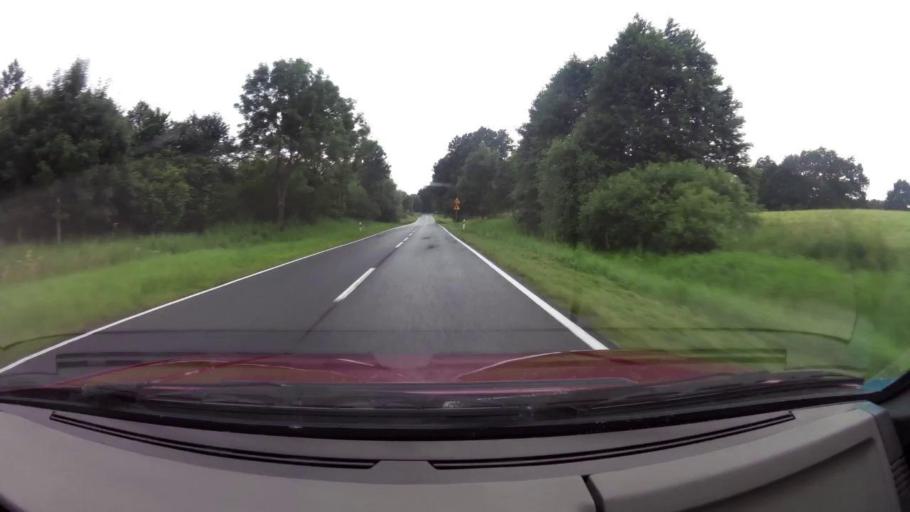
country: PL
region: West Pomeranian Voivodeship
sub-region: Powiat lobeski
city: Wegorzyno
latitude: 53.5214
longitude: 15.5073
